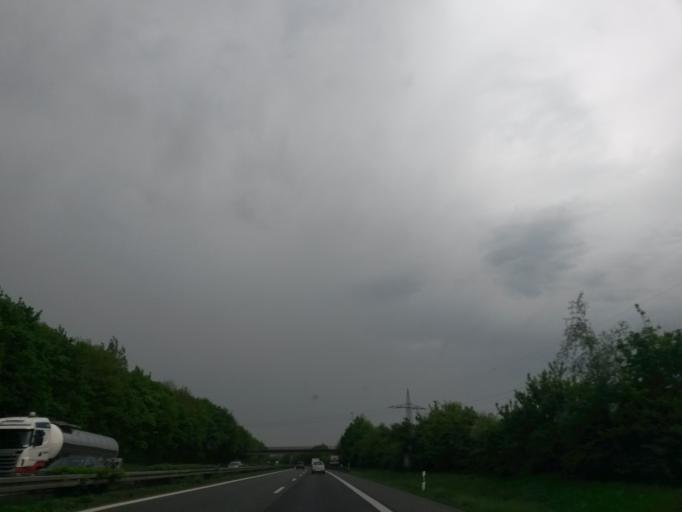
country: DE
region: Bavaria
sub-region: Upper Franconia
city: Eggolsheim
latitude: 49.7732
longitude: 11.0450
